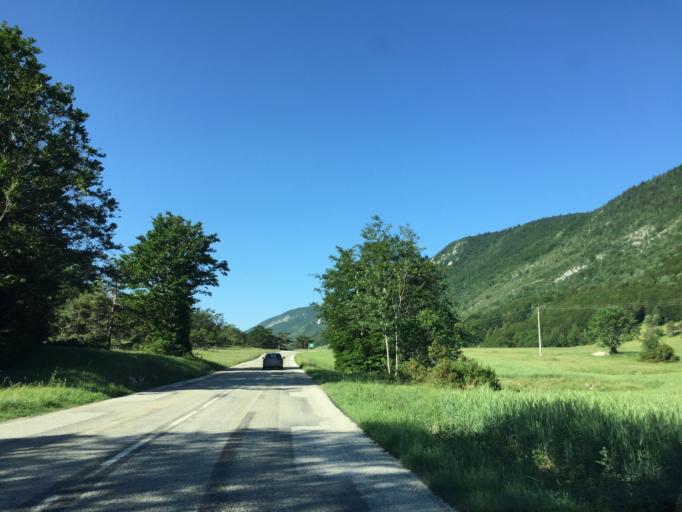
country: FR
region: Rhone-Alpes
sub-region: Departement de la Drome
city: Saint-Laurent-en-Royans
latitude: 44.9294
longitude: 5.3838
